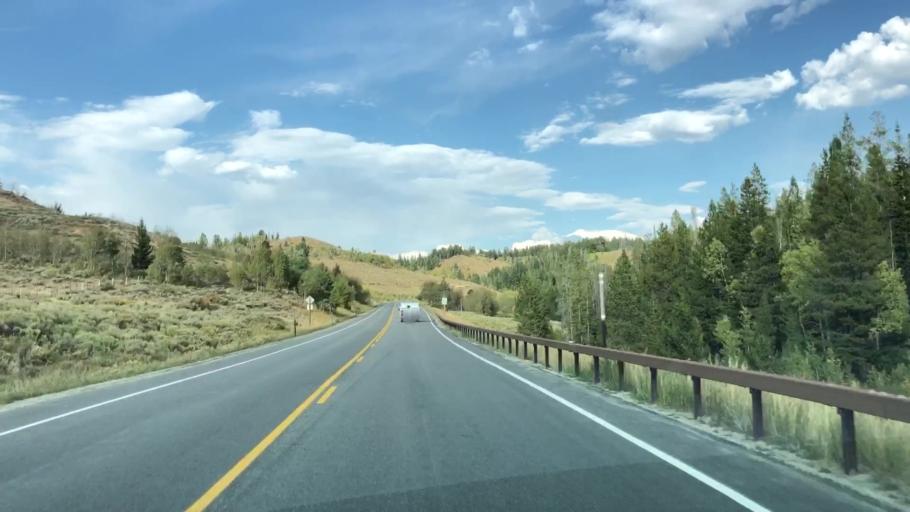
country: US
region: Wyoming
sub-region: Sublette County
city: Pinedale
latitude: 43.1365
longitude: -110.2251
